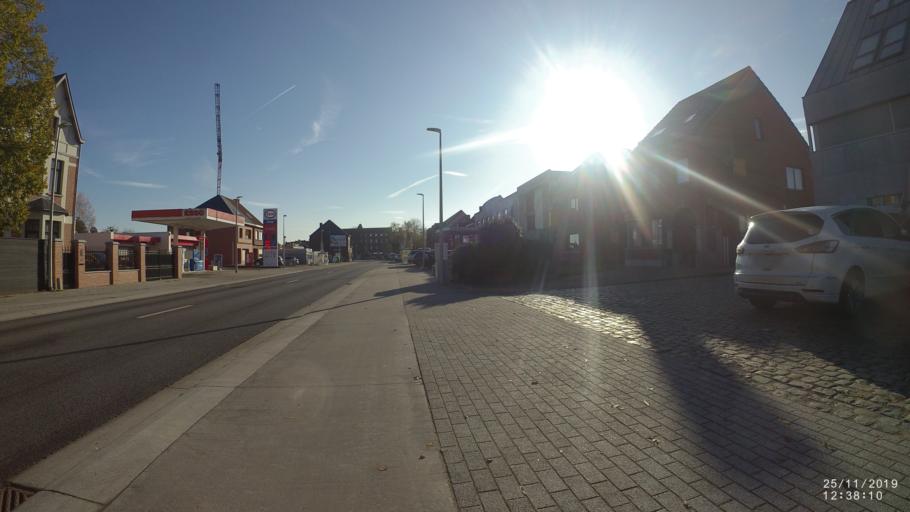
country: BE
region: Flanders
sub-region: Provincie Vlaams-Brabant
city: Aarschot
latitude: 50.9941
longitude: 4.8376
